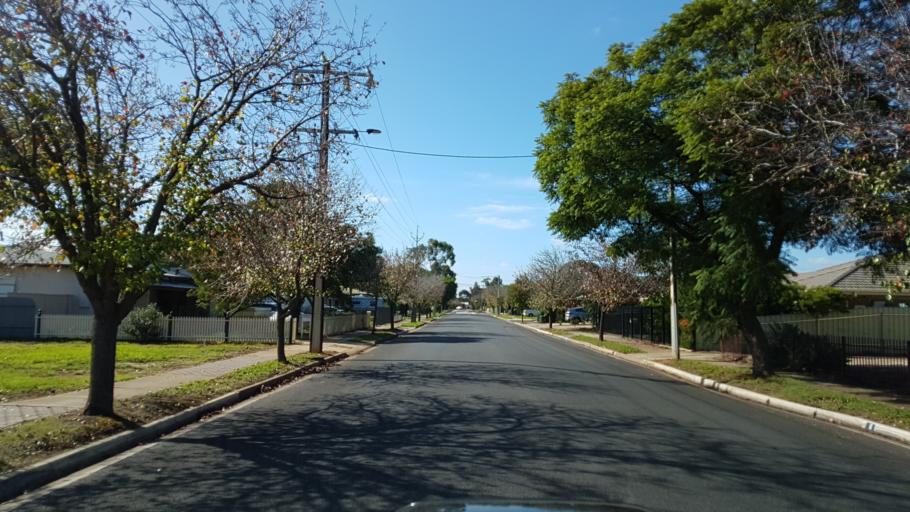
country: AU
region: South Australia
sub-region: Salisbury
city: Salisbury
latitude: -34.7560
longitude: 138.6345
